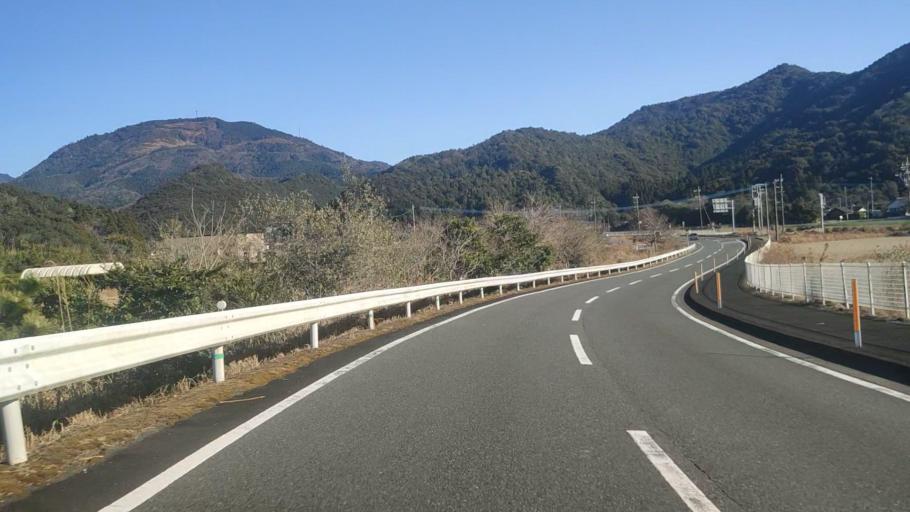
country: JP
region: Miyazaki
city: Nobeoka
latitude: 32.6786
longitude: 131.7841
